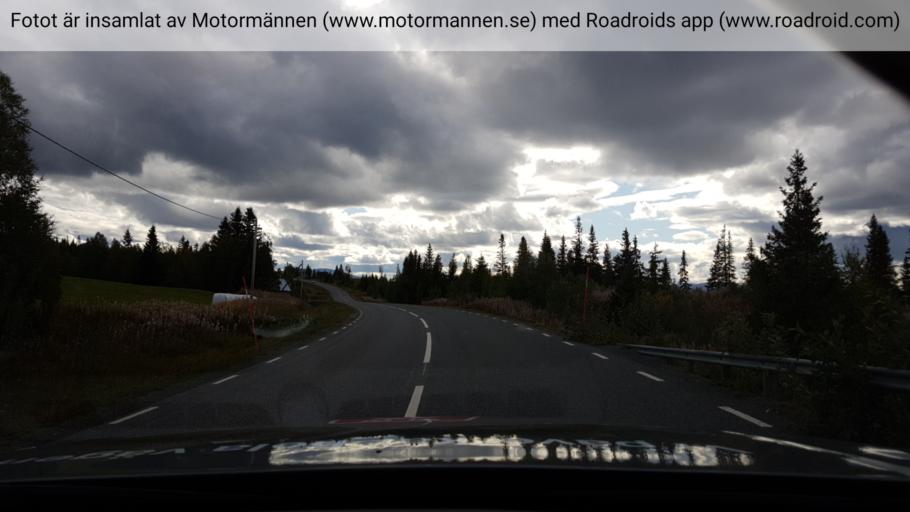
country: SE
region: Jaemtland
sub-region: Are Kommun
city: Are
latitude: 63.6688
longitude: 13.0483
